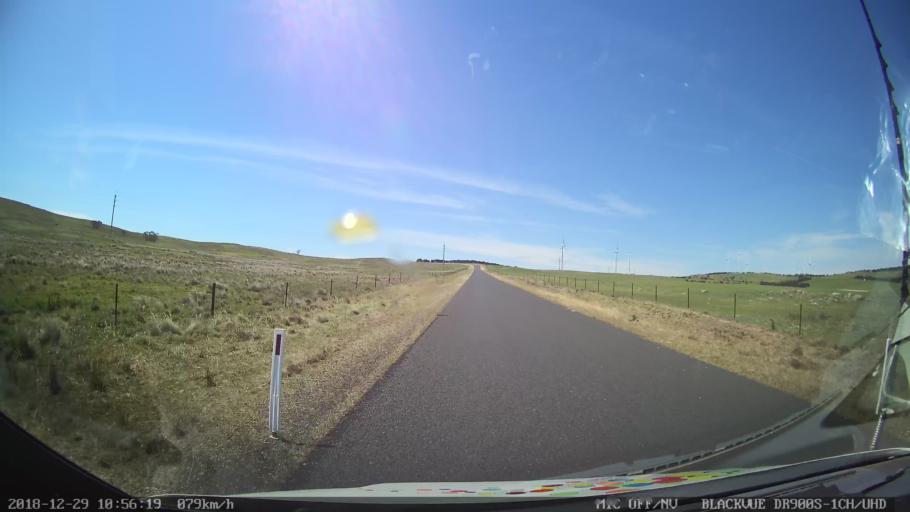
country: AU
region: New South Wales
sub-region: Palerang
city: Bungendore
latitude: -35.1330
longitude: 149.5378
